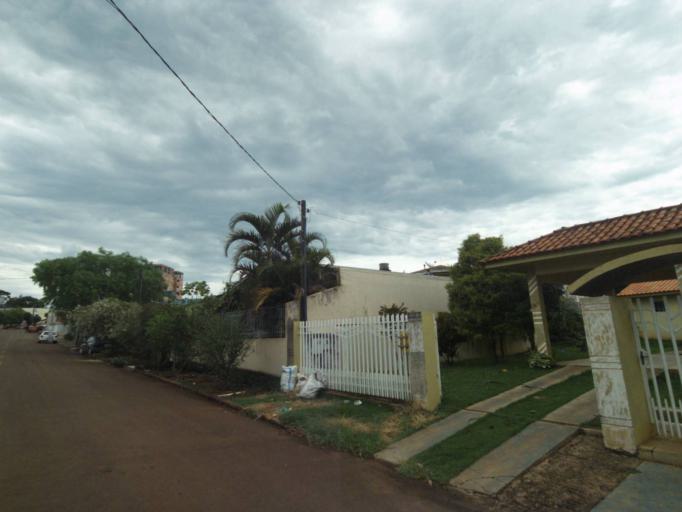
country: BR
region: Parana
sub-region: Guaraniacu
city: Guaraniacu
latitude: -25.0967
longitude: -52.8687
